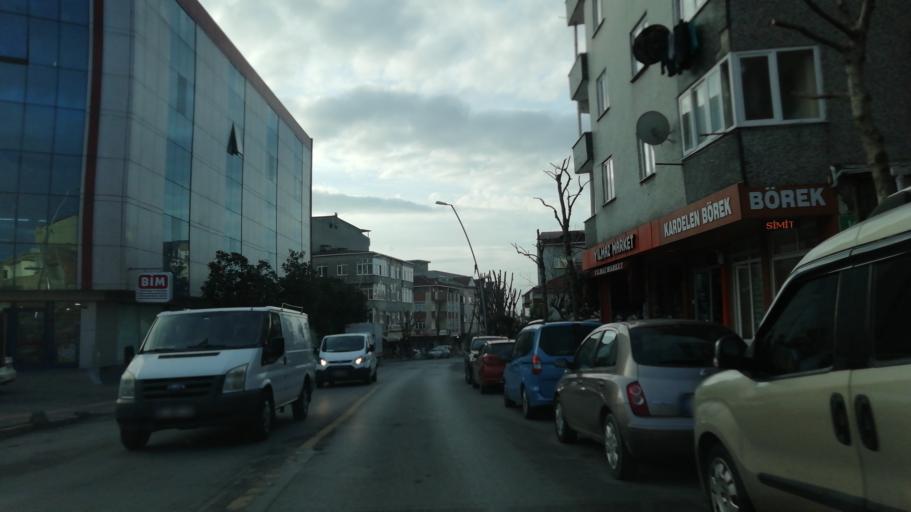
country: TR
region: Istanbul
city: Bahcelievler
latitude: 41.0094
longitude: 28.8273
